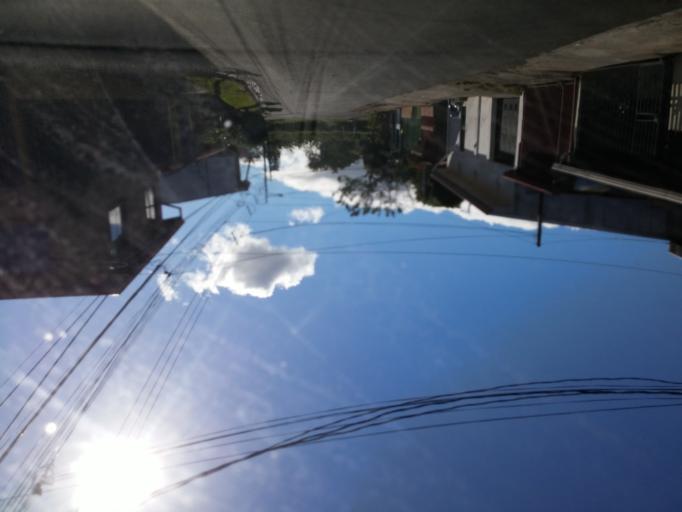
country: CR
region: Alajuela
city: Alajuela
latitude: 10.0282
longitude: -84.2036
